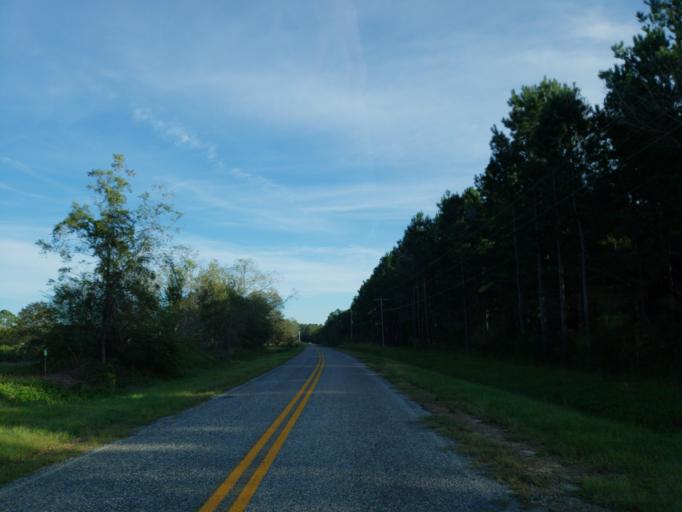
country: US
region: Georgia
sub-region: Crisp County
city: Cordele
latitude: 32.0226
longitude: -83.7391
